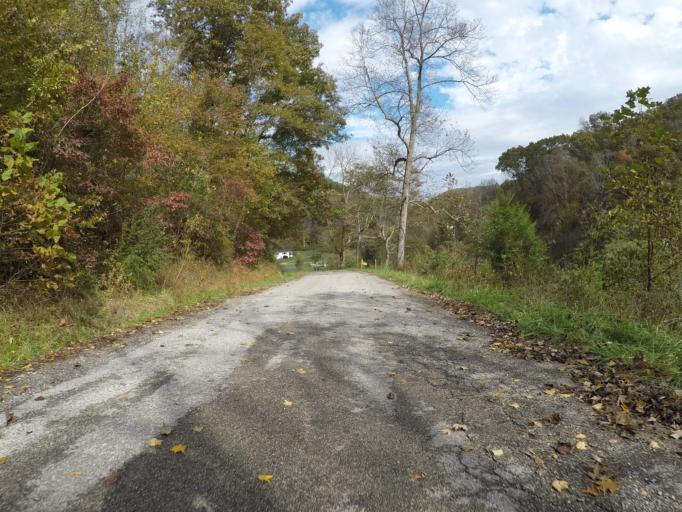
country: US
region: West Virginia
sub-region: Wayne County
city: Lavalette
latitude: 38.3490
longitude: -82.4417
